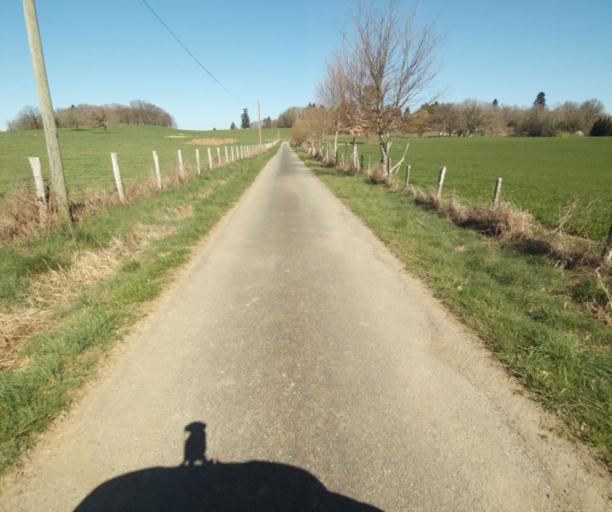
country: FR
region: Limousin
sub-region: Departement de la Correze
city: Saint-Clement
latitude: 45.3516
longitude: 1.6545
